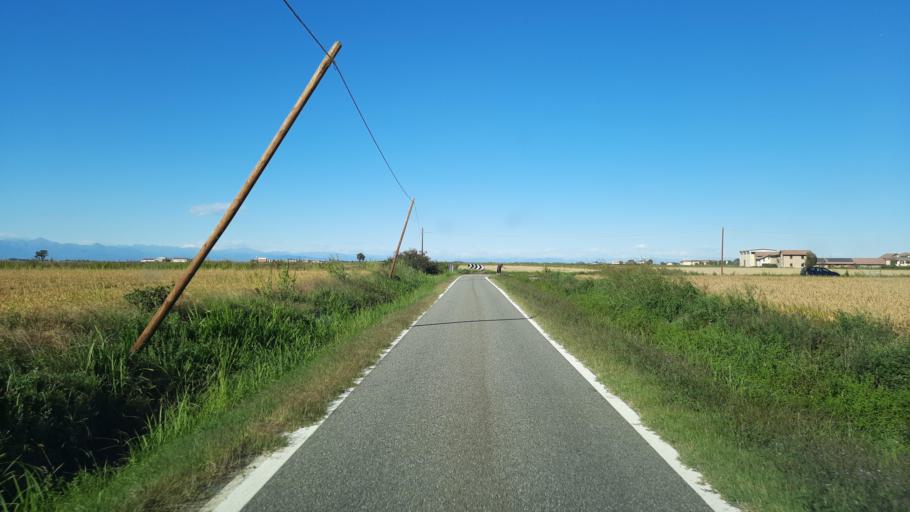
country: IT
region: Piedmont
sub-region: Provincia di Vercelli
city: Ronsecco
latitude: 45.2624
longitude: 8.2851
